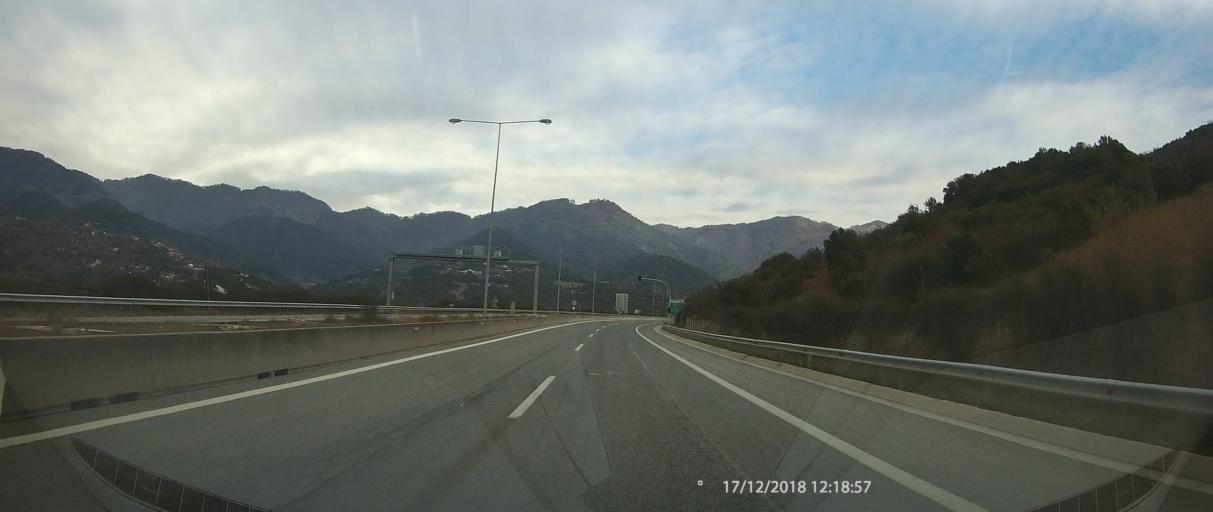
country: GR
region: Epirus
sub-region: Nomos Ioanninon
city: Metsovo
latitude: 39.7595
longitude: 21.0947
